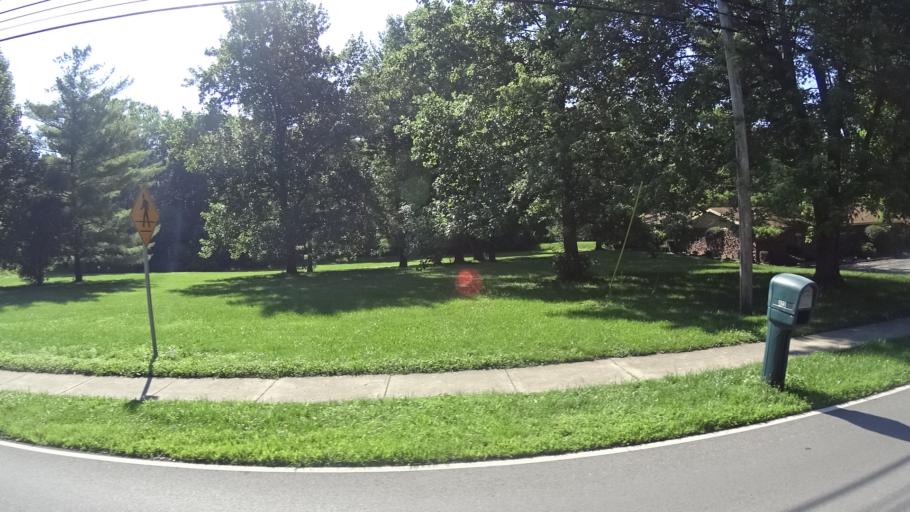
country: US
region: Indiana
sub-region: Madison County
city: Pendleton
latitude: 40.0074
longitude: -85.7443
